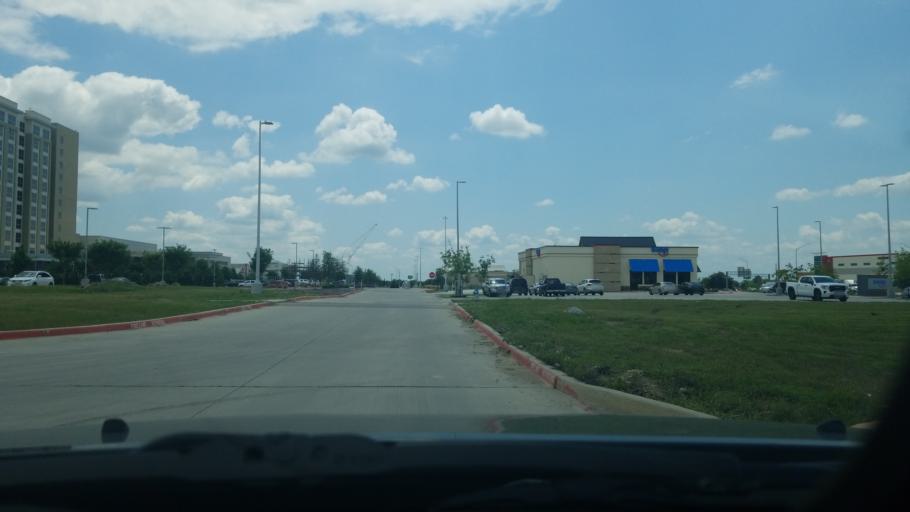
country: US
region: Texas
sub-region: Denton County
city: Denton
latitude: 33.2245
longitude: -97.1706
